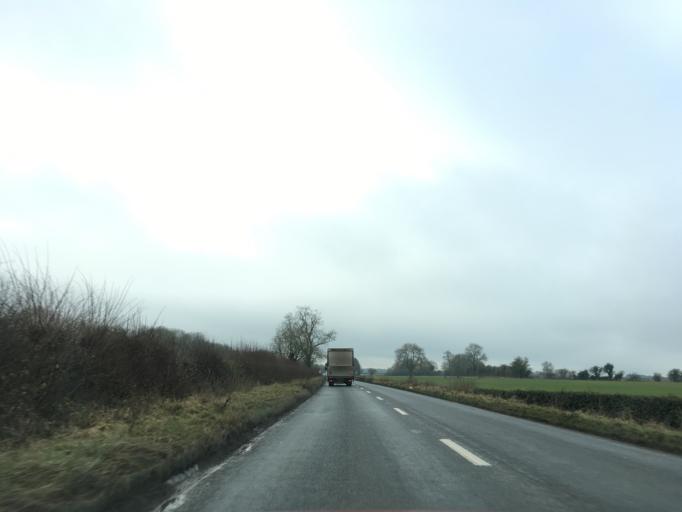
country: GB
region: England
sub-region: Gloucestershire
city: Tetbury
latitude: 51.6611
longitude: -2.1187
